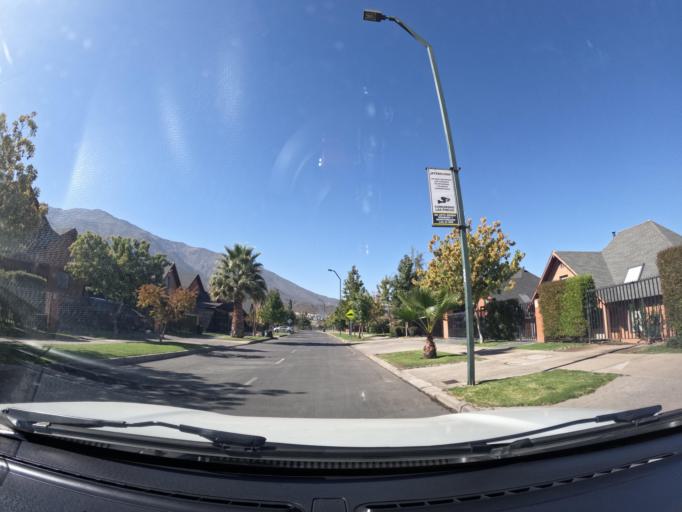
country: CL
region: Santiago Metropolitan
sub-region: Provincia de Santiago
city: Villa Presidente Frei, Nunoa, Santiago, Chile
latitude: -33.5053
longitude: -70.5266
